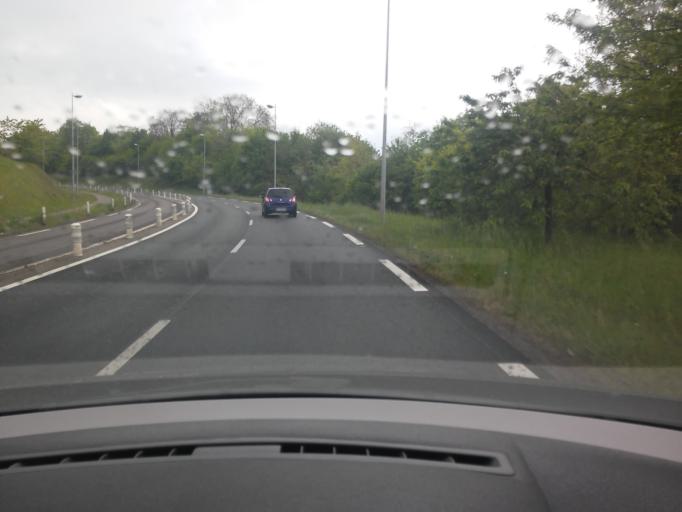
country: FR
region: Lorraine
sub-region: Departement de Meurthe-et-Moselle
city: Laxou
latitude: 48.6839
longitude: 6.1392
